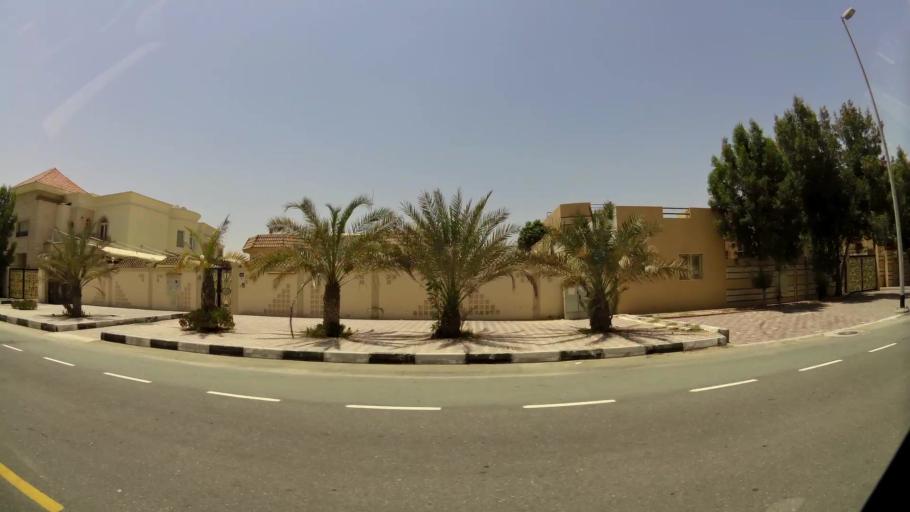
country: AE
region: Dubai
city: Dubai
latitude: 25.0840
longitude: 55.2048
